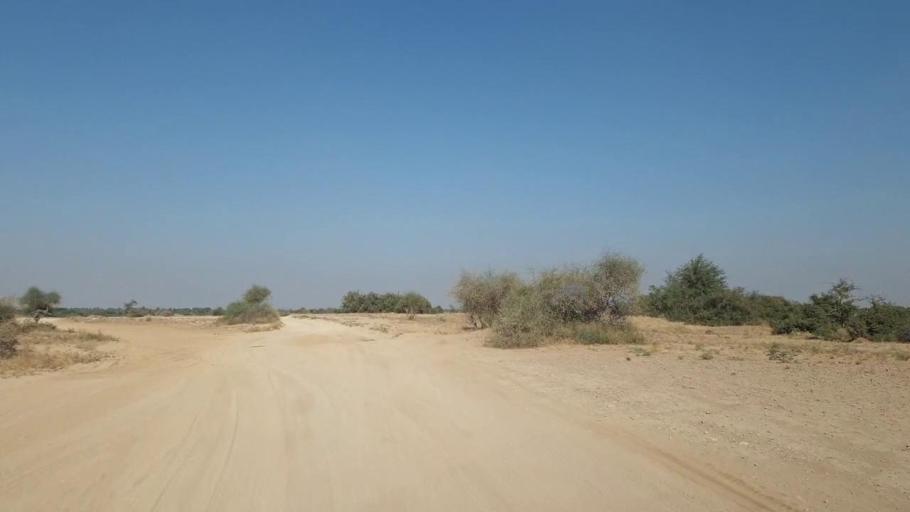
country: PK
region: Sindh
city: Jamshoro
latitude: 25.2775
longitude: 67.8074
